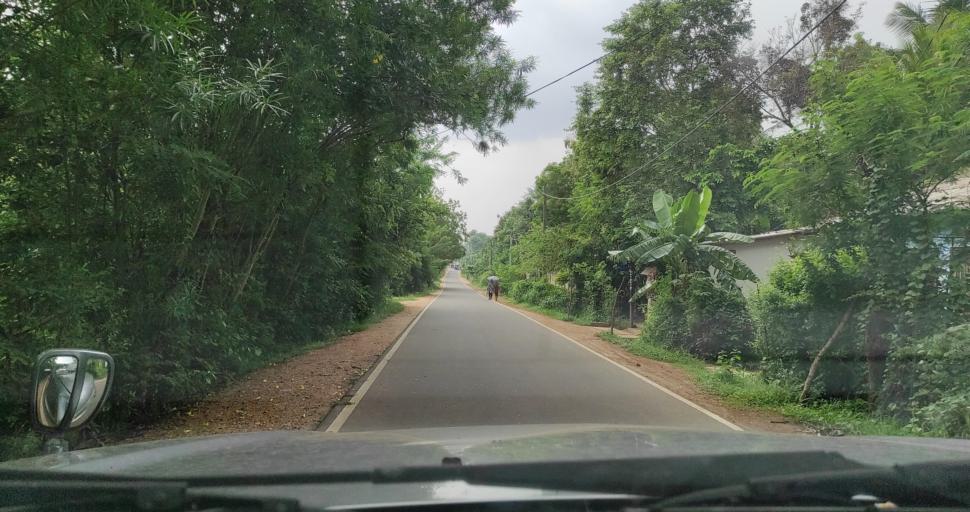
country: LK
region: Eastern Province
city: Trincomalee
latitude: 8.3704
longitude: 81.0107
